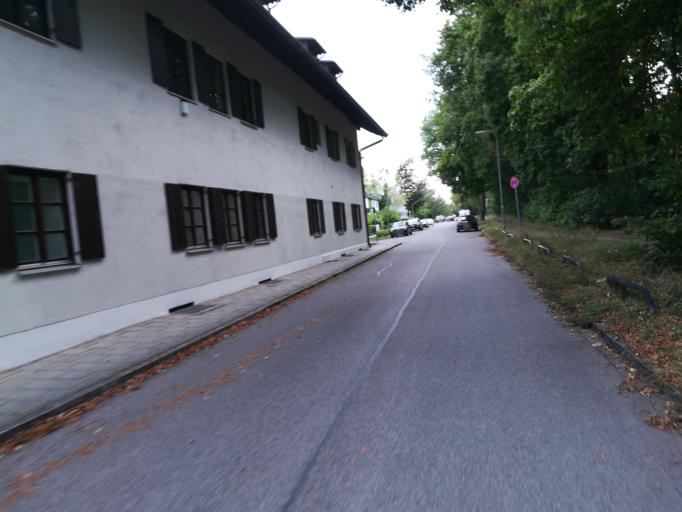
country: DE
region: Bavaria
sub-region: Upper Bavaria
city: Munich
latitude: 48.1630
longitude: 11.5208
